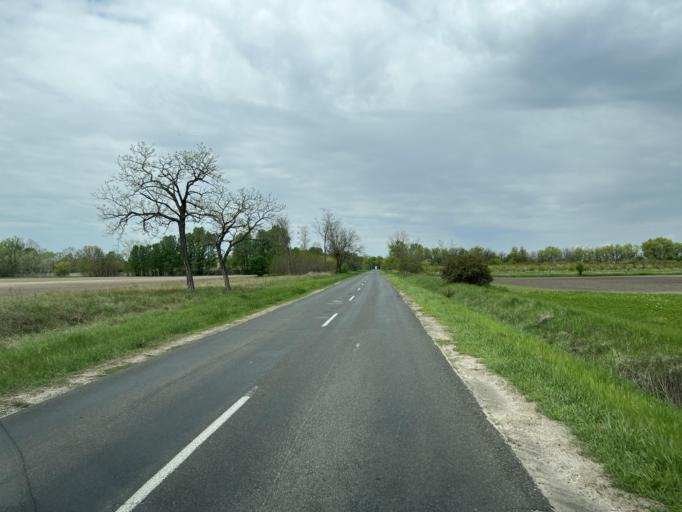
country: HU
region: Pest
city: Cegled
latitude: 47.1584
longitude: 19.8493
